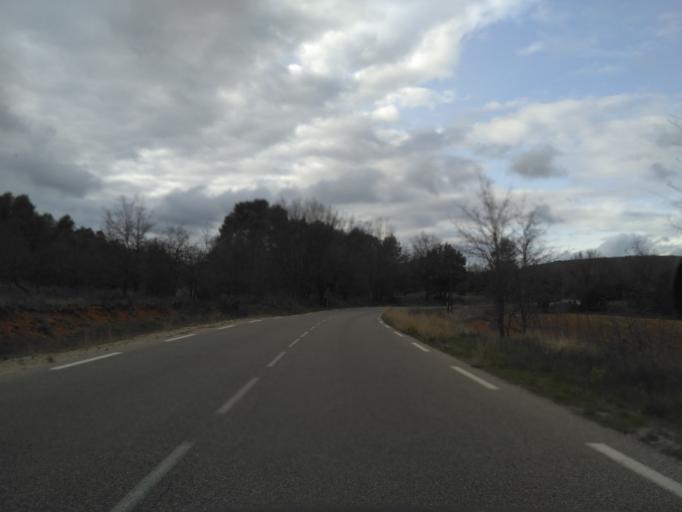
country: FR
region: Provence-Alpes-Cote d'Azur
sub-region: Departement du Var
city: Barjols
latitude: 43.5750
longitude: 6.0167
